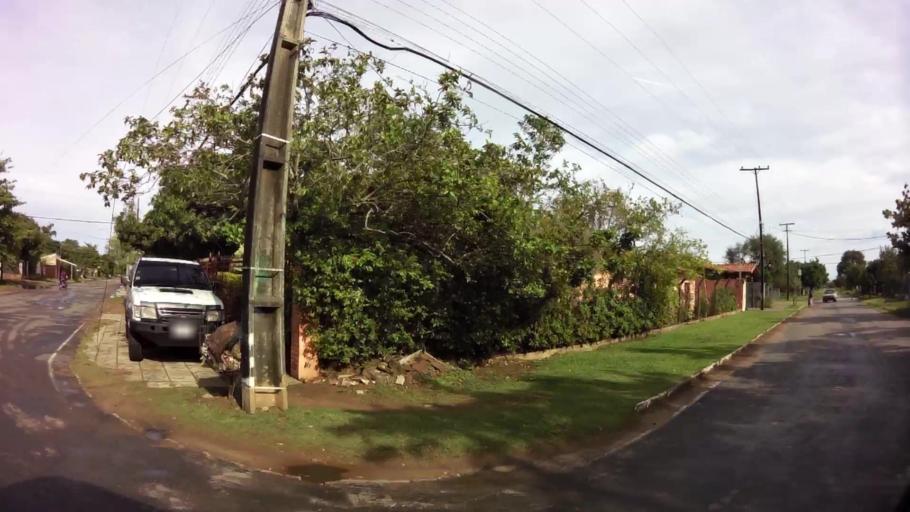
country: PY
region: Central
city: Limpio
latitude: -25.1687
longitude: -57.4836
